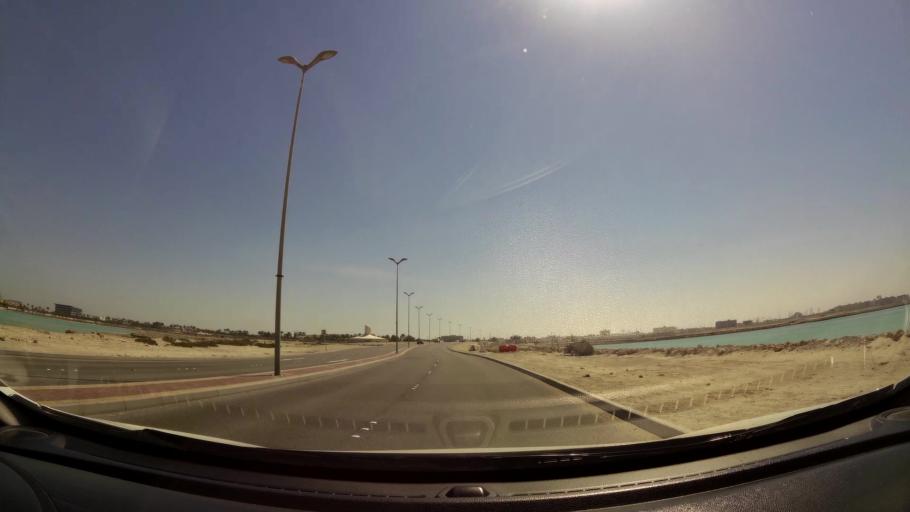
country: BH
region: Muharraq
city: Al Hadd
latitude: 26.2855
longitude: 50.6595
